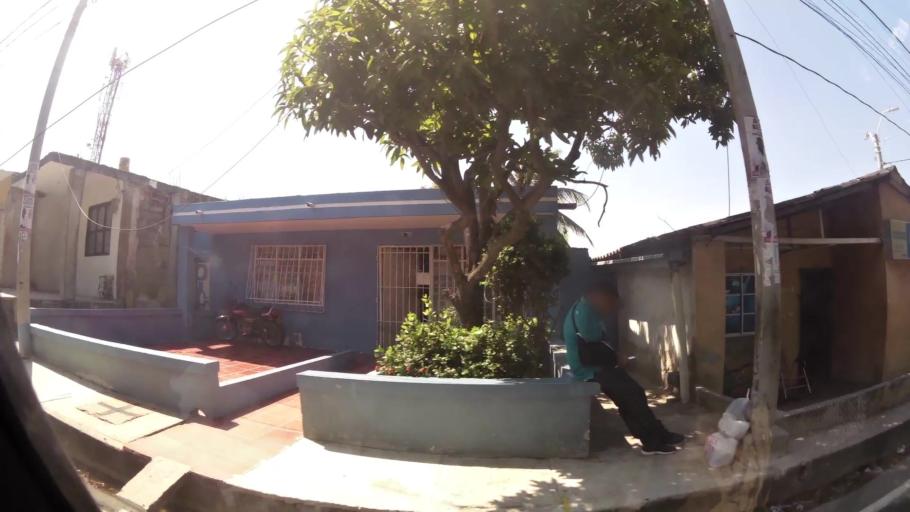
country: CO
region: Atlantico
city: Barranquilla
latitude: 10.9710
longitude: -74.8252
